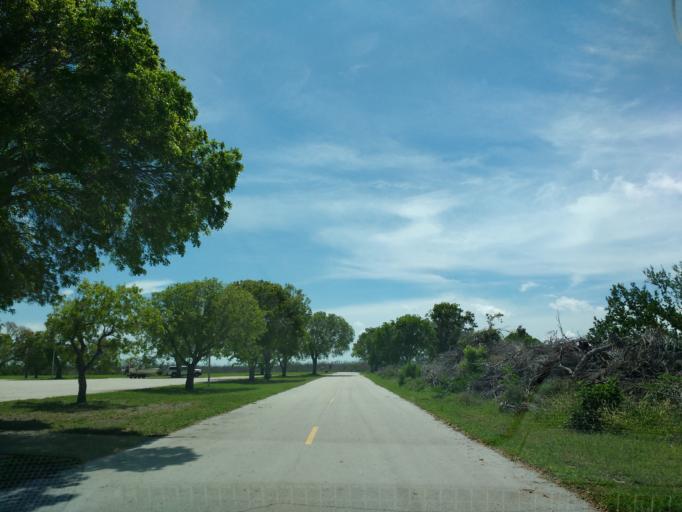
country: US
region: Florida
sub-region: Monroe County
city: Islamorada
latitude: 25.1446
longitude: -80.9231
